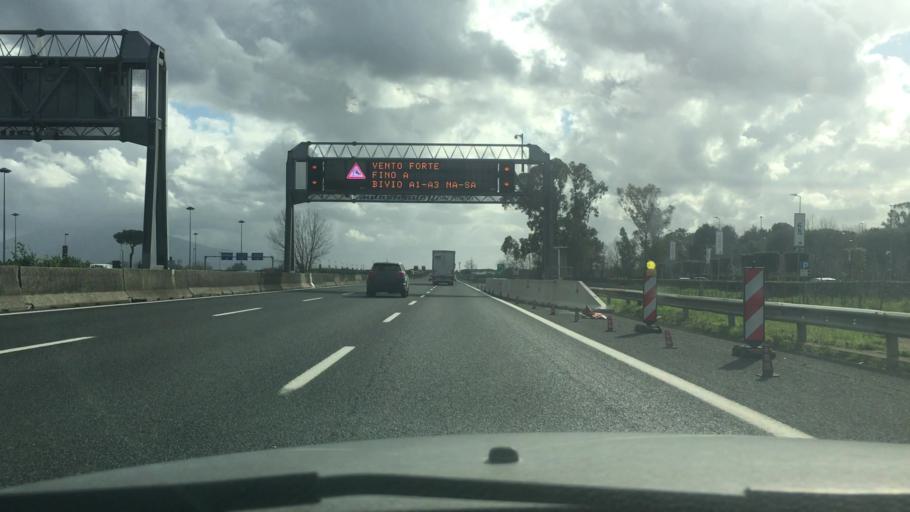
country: IT
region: Campania
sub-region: Provincia di Caserta
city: Marcianise
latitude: 41.0066
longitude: 14.3232
